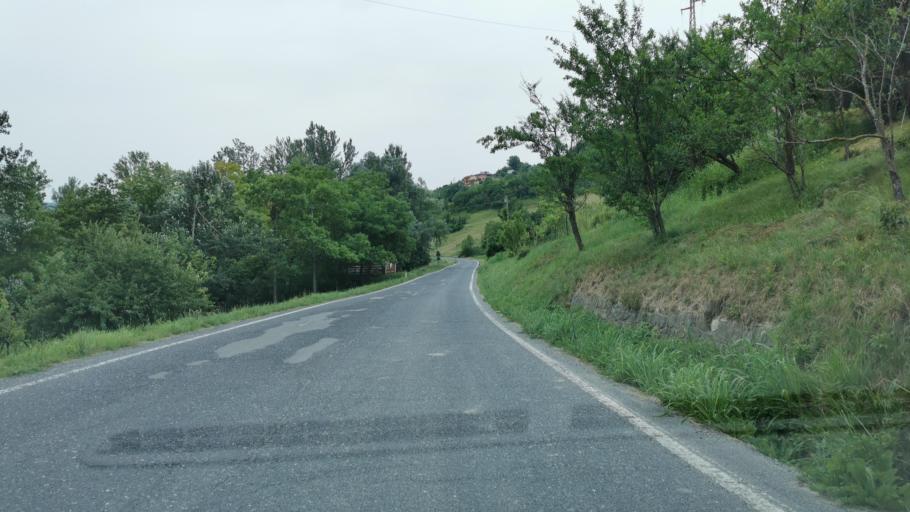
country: IT
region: Piedmont
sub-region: Provincia di Cuneo
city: Ceva
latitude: 44.3939
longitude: 8.0476
